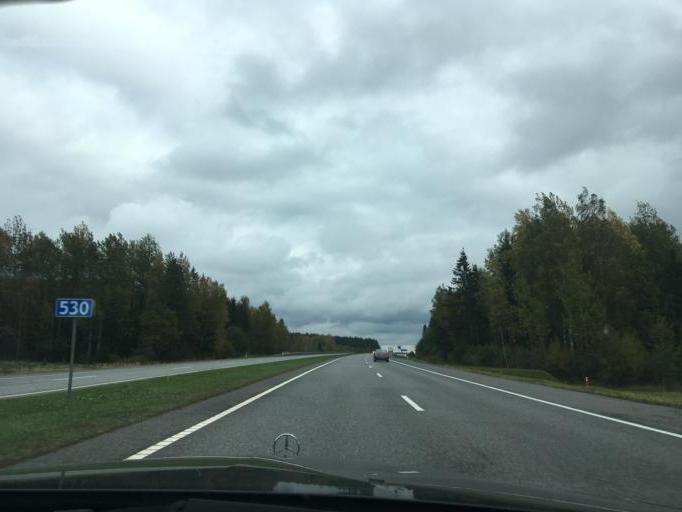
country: BY
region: Vitebsk
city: Talachyn
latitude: 54.4790
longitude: 29.8409
